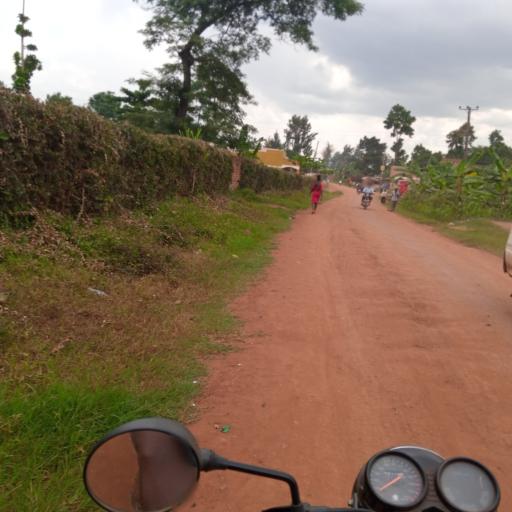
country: UG
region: Eastern Region
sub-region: Mbale District
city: Mbale
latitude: 1.1076
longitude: 34.1772
